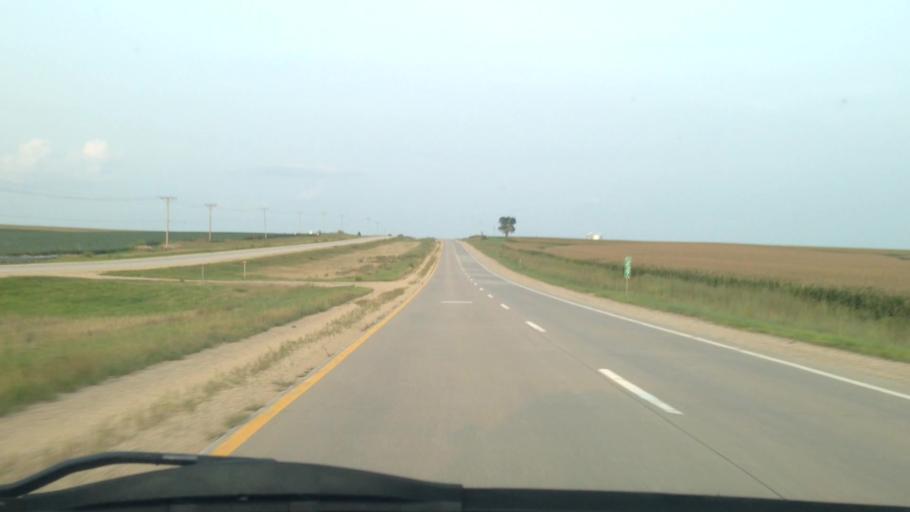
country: US
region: Iowa
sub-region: Benton County
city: Atkins
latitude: 41.9632
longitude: -91.9653
